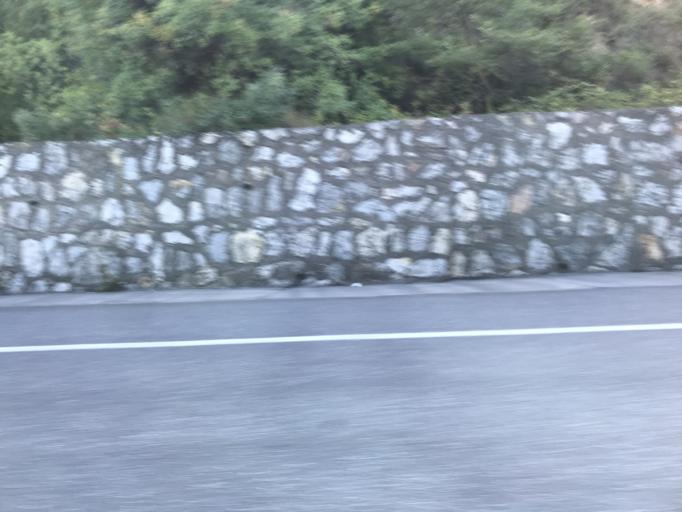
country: TR
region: Kocaeli
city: Gebze
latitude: 40.7732
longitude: 29.4247
